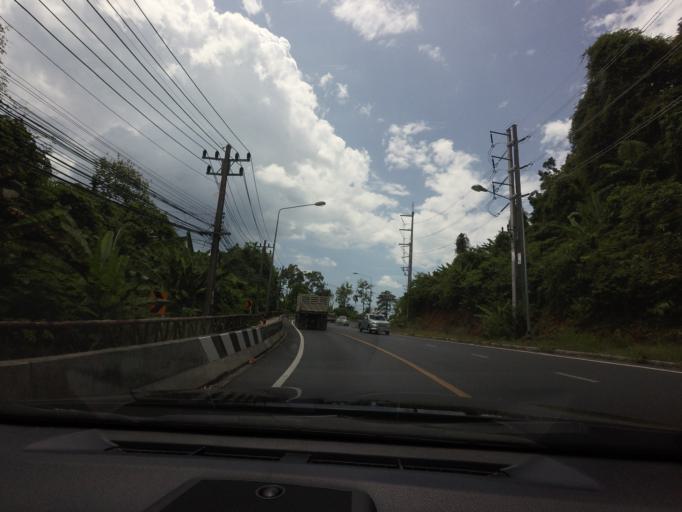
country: TH
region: Phangnga
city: Ban Khao Lak
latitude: 8.6341
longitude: 98.2460
